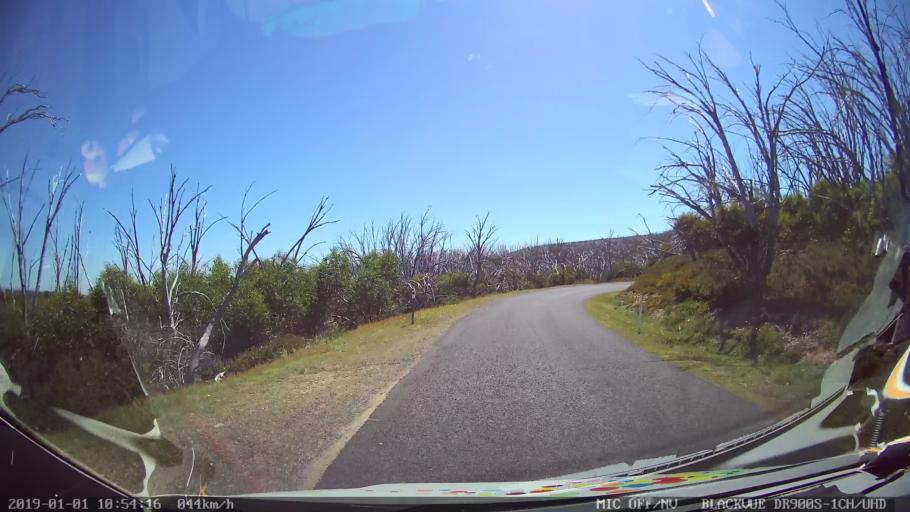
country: AU
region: New South Wales
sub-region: Snowy River
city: Jindabyne
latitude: -36.0097
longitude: 148.3834
